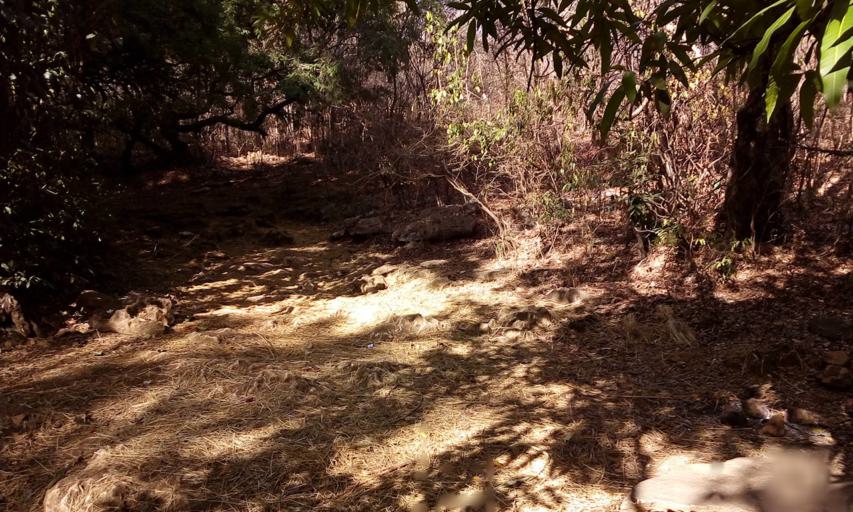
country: MG
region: Melaky
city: Mahabe
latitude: -16.3827
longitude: 45.3424
